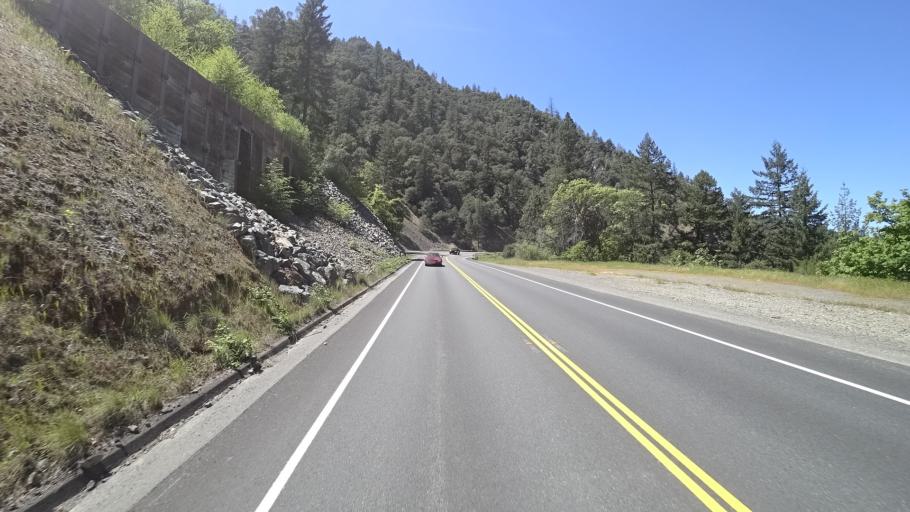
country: US
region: California
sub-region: Humboldt County
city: Willow Creek
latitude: 40.7902
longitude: -123.4527
